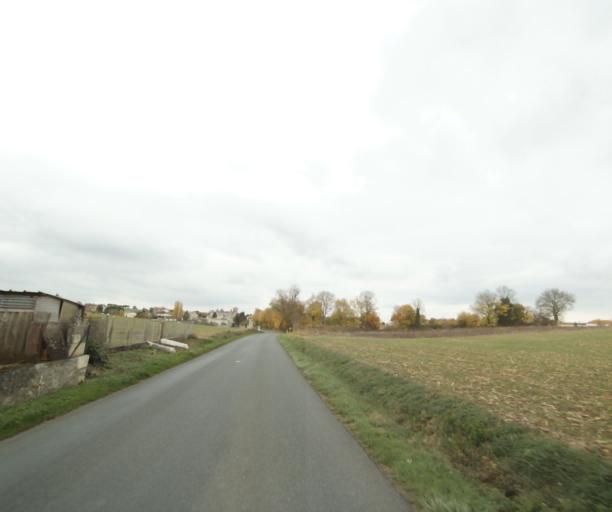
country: FR
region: Poitou-Charentes
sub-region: Departement de la Charente-Maritime
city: Bussac-sur-Charente
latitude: 45.7792
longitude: -0.6732
